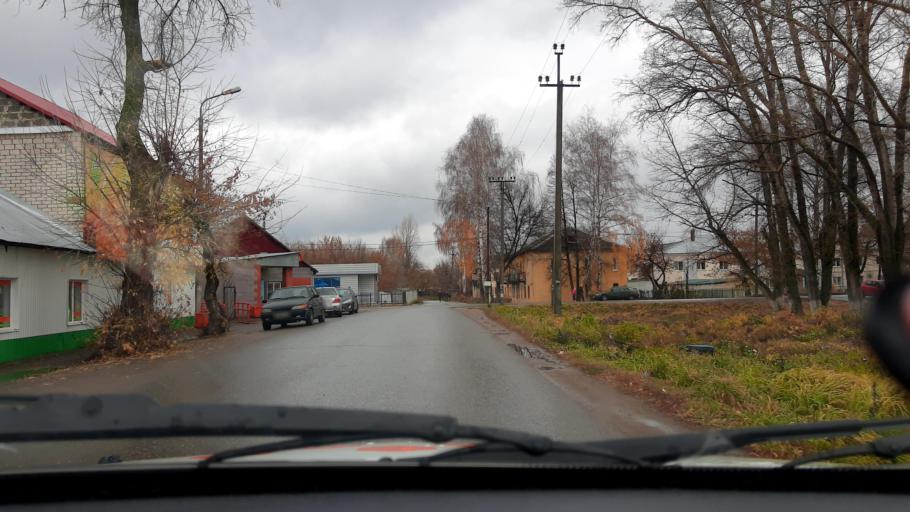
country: RU
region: Bashkortostan
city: Iglino
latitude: 54.7708
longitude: 56.2252
